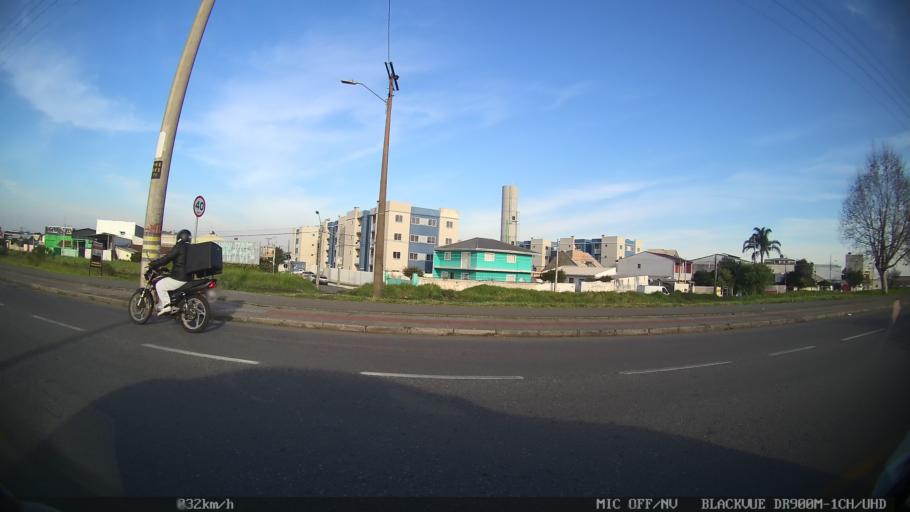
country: BR
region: Parana
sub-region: Pinhais
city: Pinhais
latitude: -25.4412
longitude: -49.1821
